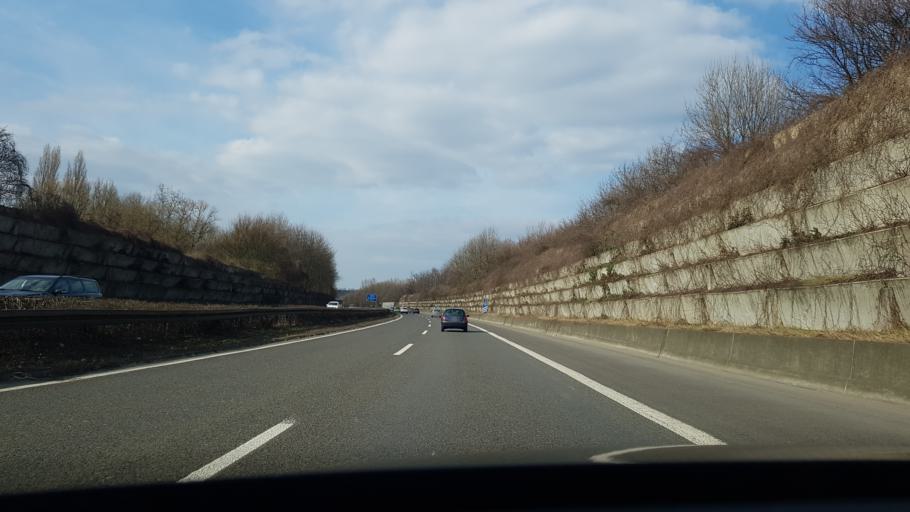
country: DE
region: North Rhine-Westphalia
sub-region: Regierungsbezirk Dusseldorf
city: Dinslaken
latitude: 51.5197
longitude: 6.7602
